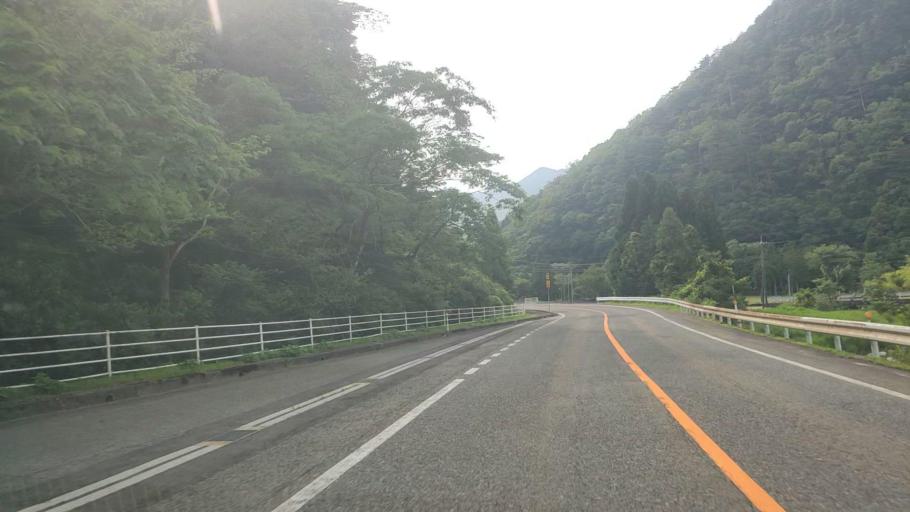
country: JP
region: Tottori
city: Kurayoshi
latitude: 35.3181
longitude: 133.8485
